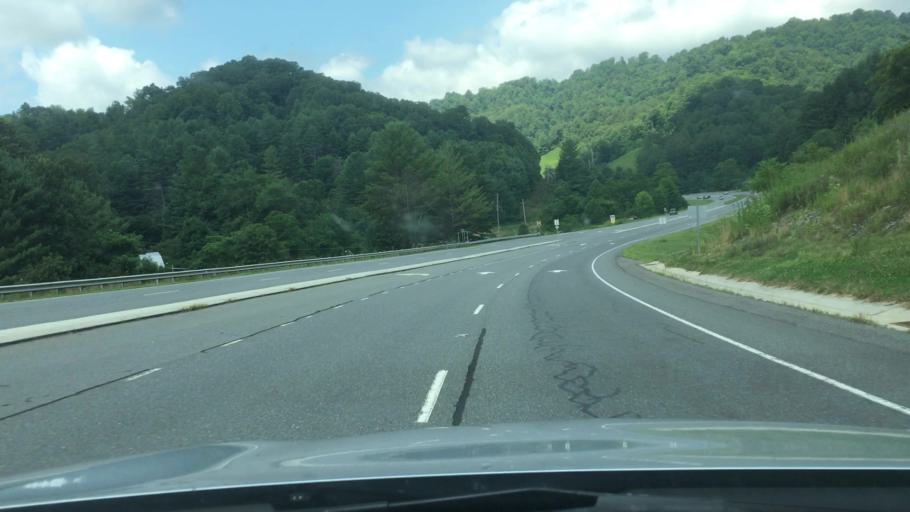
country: US
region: North Carolina
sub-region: Madison County
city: Mars Hill
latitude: 35.9135
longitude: -82.4554
